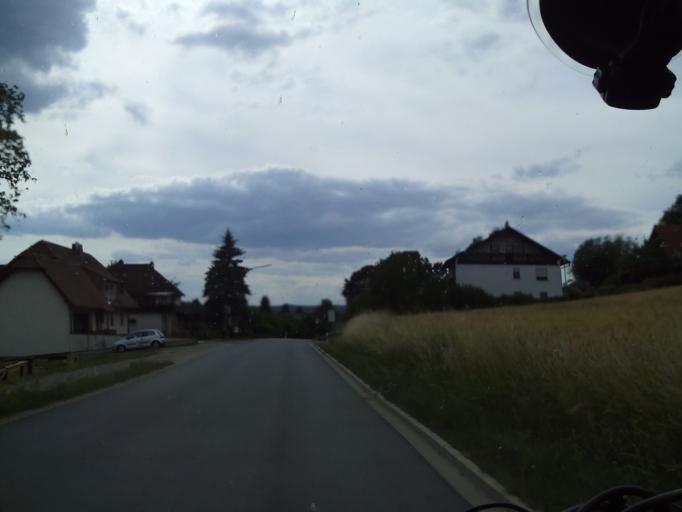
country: DE
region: Bavaria
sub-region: Regierungsbezirk Unterfranken
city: Untermerzbach
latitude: 50.1023
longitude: 10.9037
